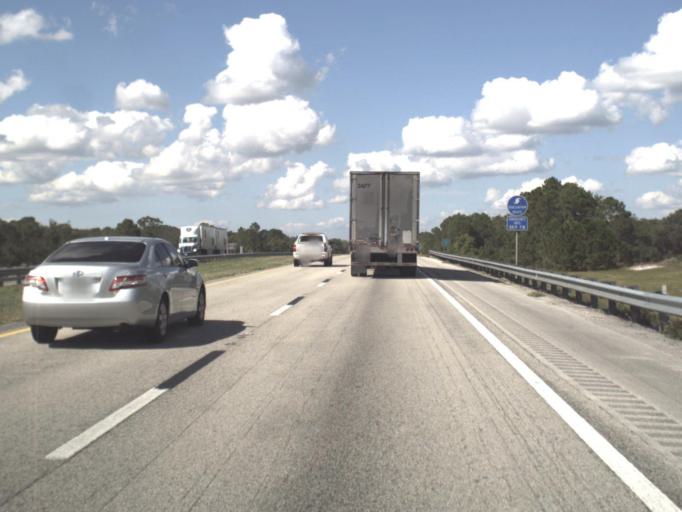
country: US
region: Florida
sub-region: Indian River County
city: Fellsmere
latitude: 27.6635
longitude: -80.8716
